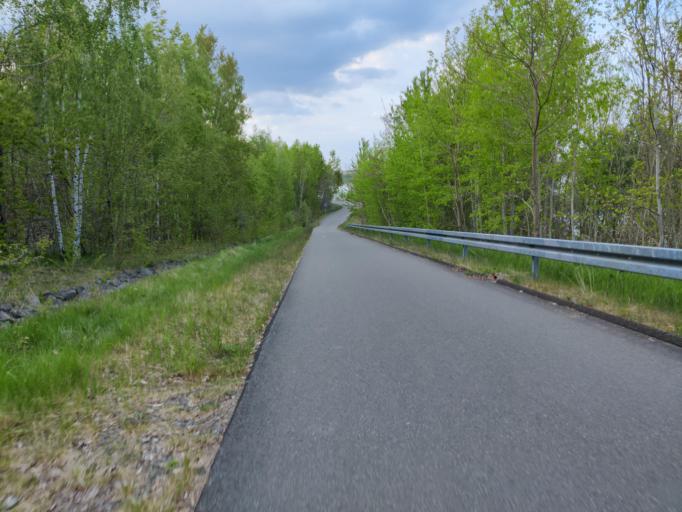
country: DE
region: Saxony
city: Rotha
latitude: 51.2215
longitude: 12.4292
